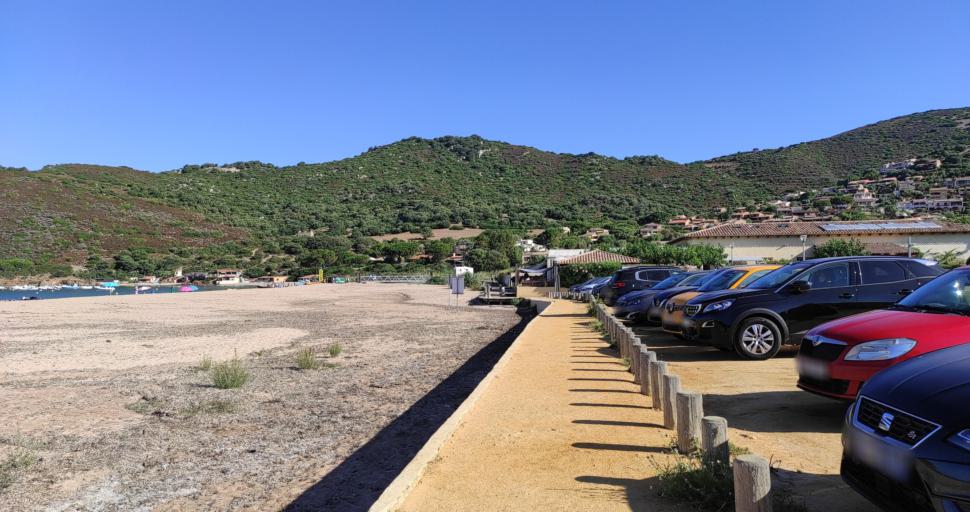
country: FR
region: Corsica
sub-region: Departement de la Corse-du-Sud
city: Alata
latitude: 41.9913
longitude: 8.6696
